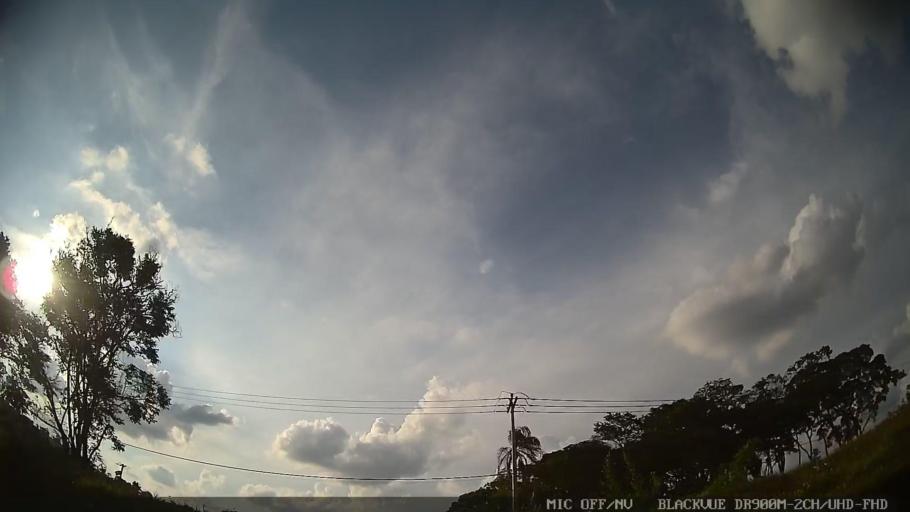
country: BR
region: Sao Paulo
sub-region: Braganca Paulista
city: Braganca Paulista
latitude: -22.9209
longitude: -46.5001
